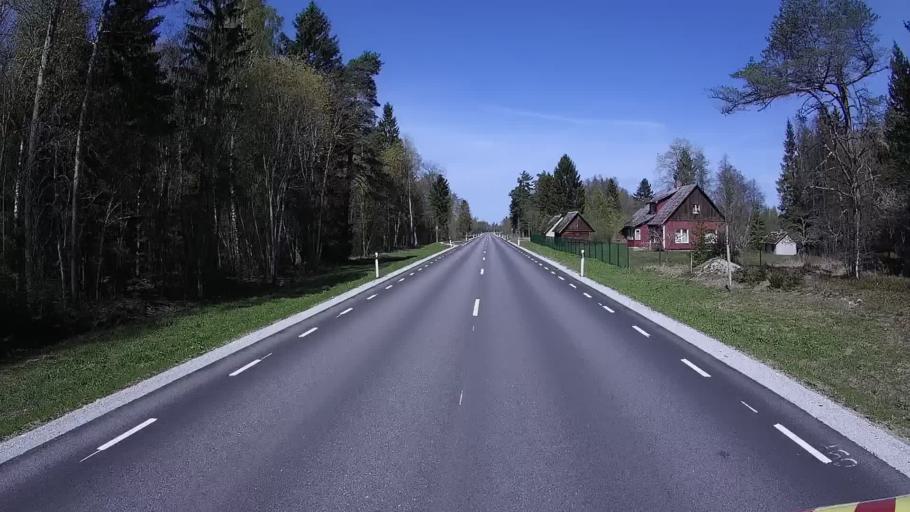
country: EE
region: Harju
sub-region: Nissi vald
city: Turba
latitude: 59.1509
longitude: 24.0770
